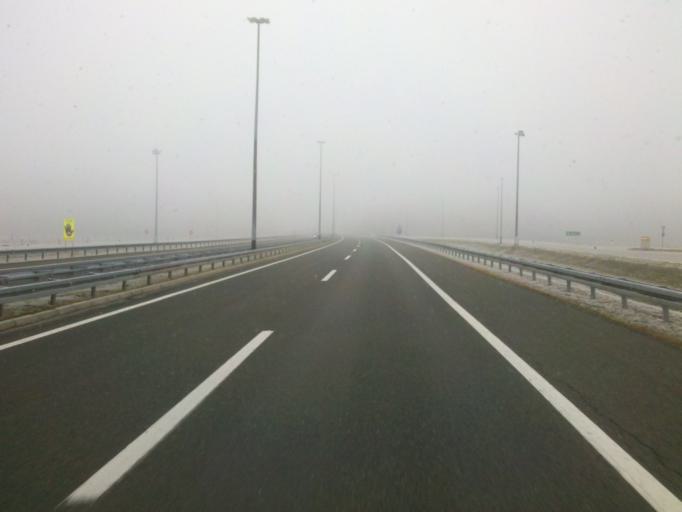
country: HR
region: Varazdinska
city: Jalzabet
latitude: 46.2843
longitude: 16.4564
